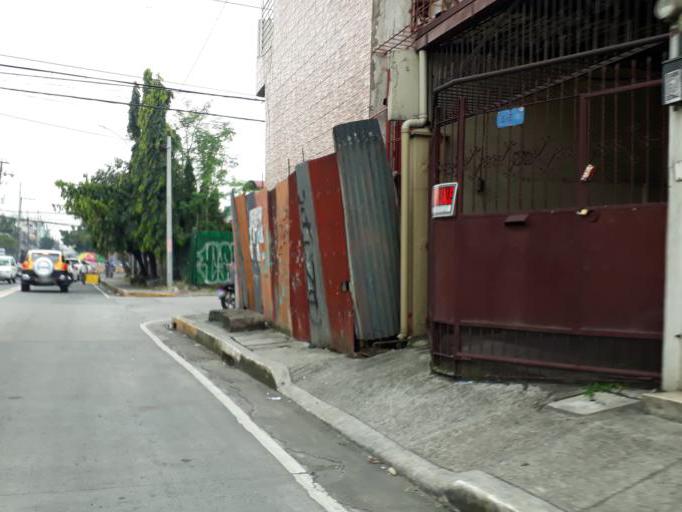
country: PH
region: Calabarzon
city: Bagong Pagasa
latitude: 14.6610
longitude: 121.0375
